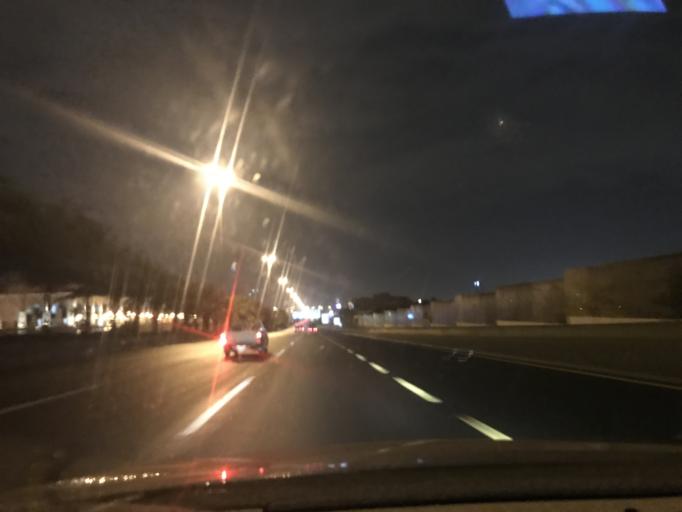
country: SA
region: Ar Riyad
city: Riyadh
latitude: 24.7446
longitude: 46.6087
